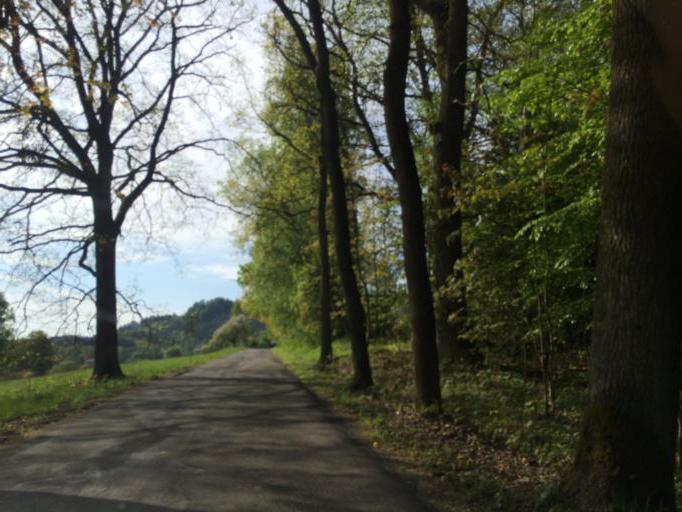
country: CZ
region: Central Bohemia
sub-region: Okres Mlada Boleslav
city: Zd'ar
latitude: 50.5346
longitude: 15.0713
